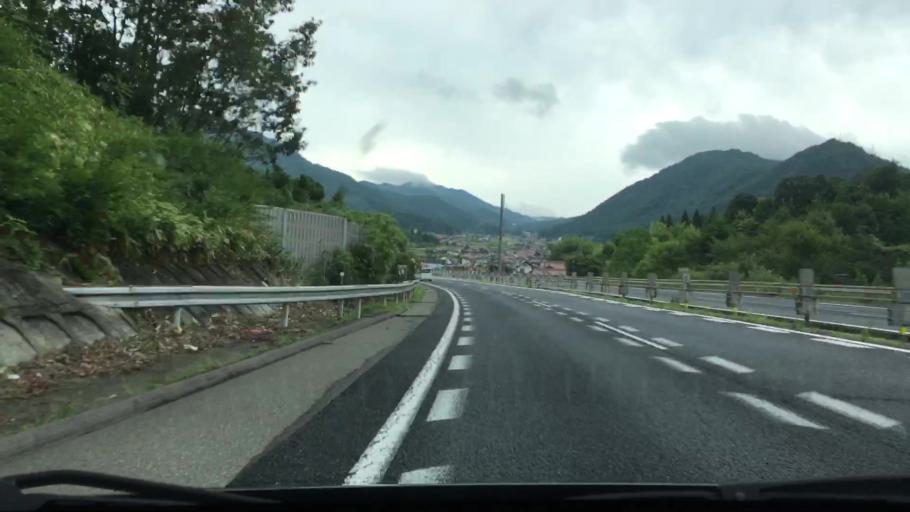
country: JP
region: Hiroshima
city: Hiroshima-shi
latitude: 34.6508
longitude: 132.5172
